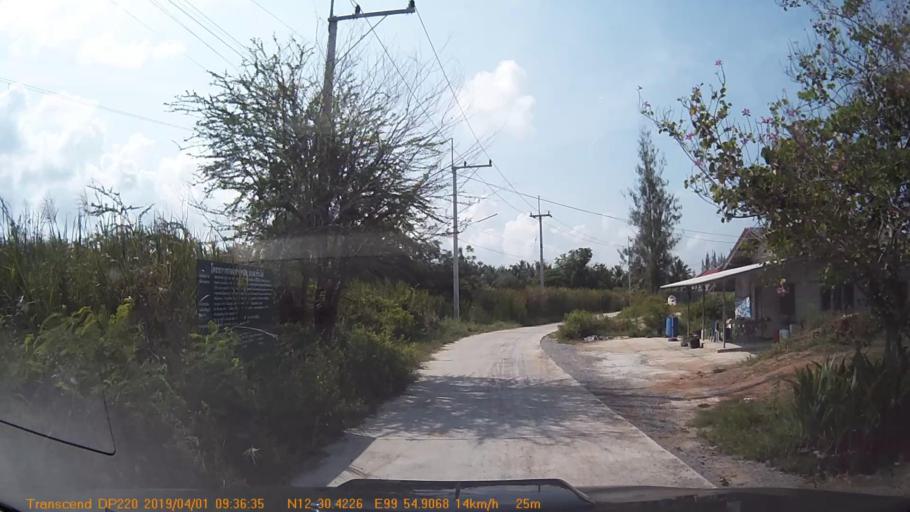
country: TH
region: Prachuap Khiri Khan
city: Hua Hin
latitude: 12.5073
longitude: 99.9152
